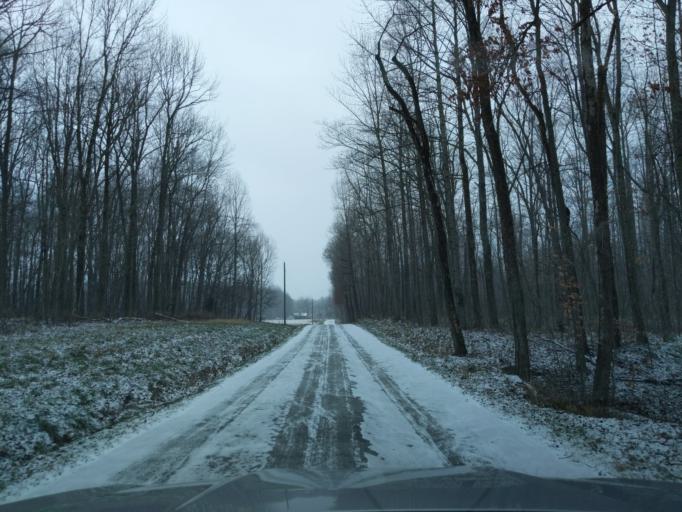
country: US
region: Indiana
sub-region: Decatur County
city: Westport
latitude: 39.2339
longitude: -85.4895
